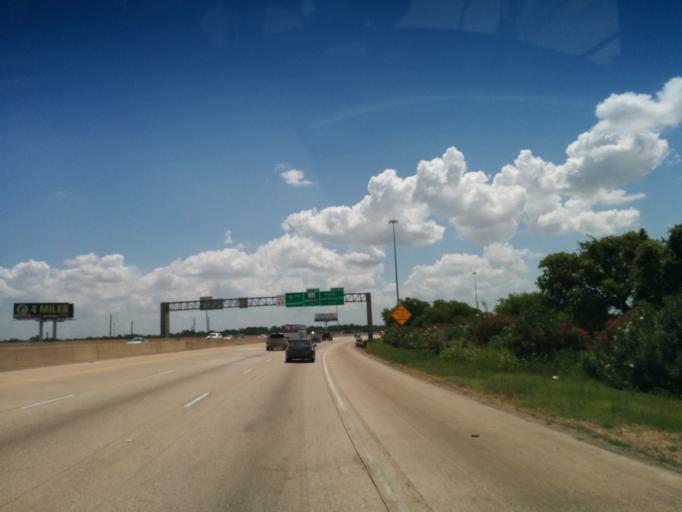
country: US
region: Texas
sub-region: Harris County
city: Highlands
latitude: 29.7952
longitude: -95.0706
